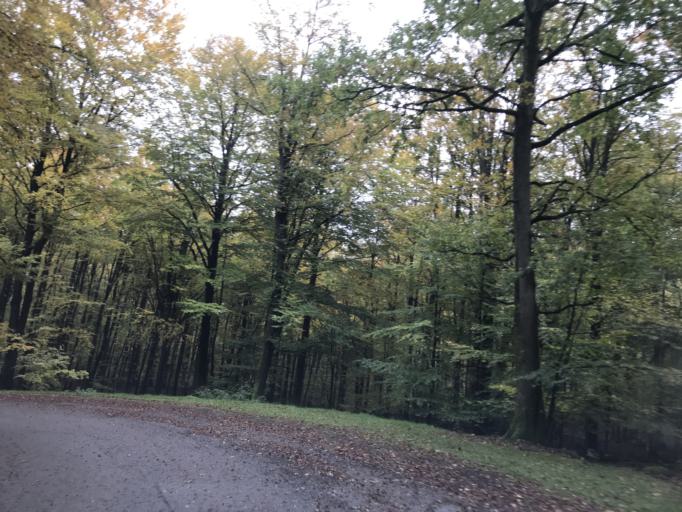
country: SE
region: Skane
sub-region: Klippans Kommun
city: Ljungbyhed
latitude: 56.0282
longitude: 13.2560
